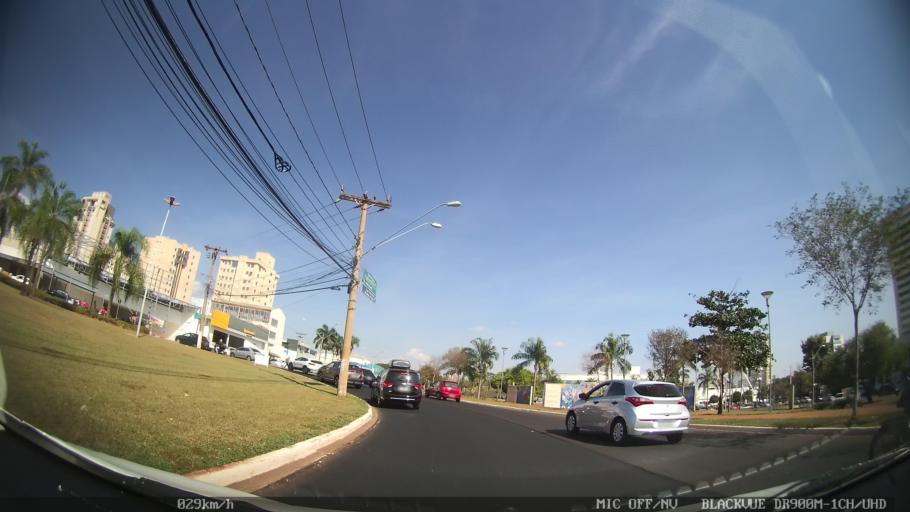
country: BR
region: Sao Paulo
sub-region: Ribeirao Preto
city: Ribeirao Preto
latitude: -21.2094
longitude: -47.8129
